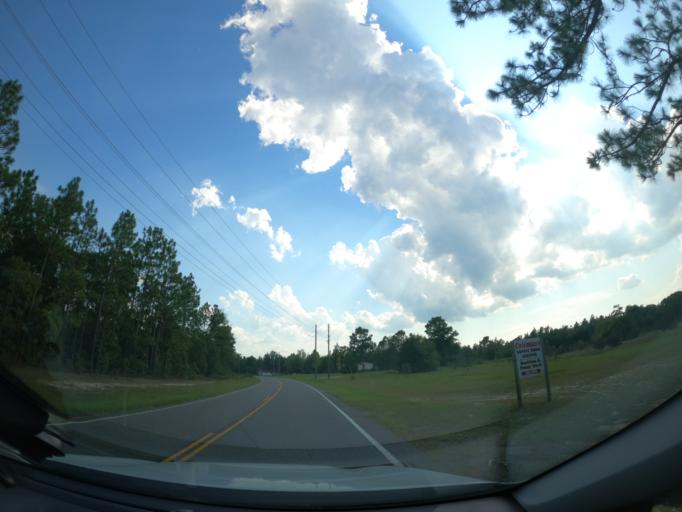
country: US
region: South Carolina
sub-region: Barnwell County
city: Williston
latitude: 33.5171
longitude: -81.5037
